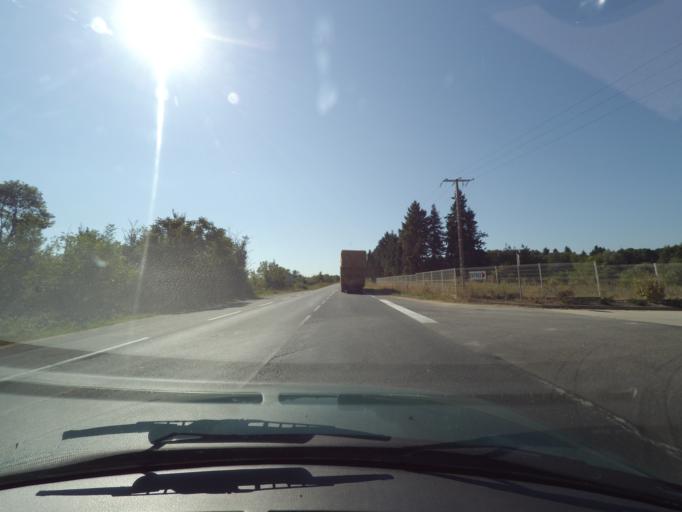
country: FR
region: Poitou-Charentes
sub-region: Departement de la Vienne
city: Lussac-les-Chateaux
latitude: 46.4110
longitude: 0.6888
